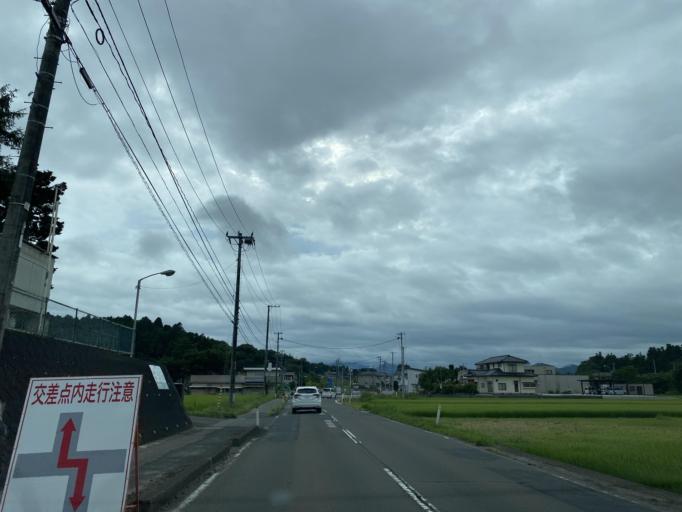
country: JP
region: Miyagi
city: Tomiya
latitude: 38.3951
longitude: 140.8992
